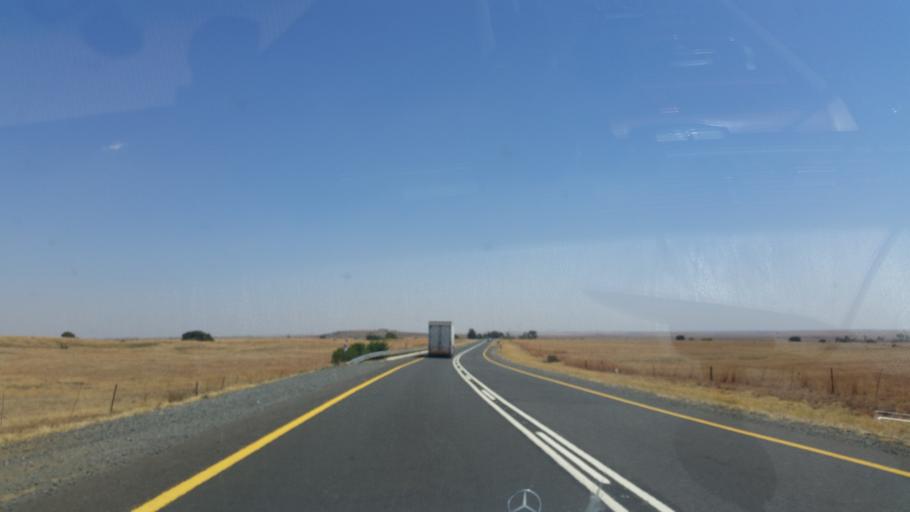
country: ZA
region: Orange Free State
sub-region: Lejweleputswa District Municipality
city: Winburg
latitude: -28.4979
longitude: 27.0454
